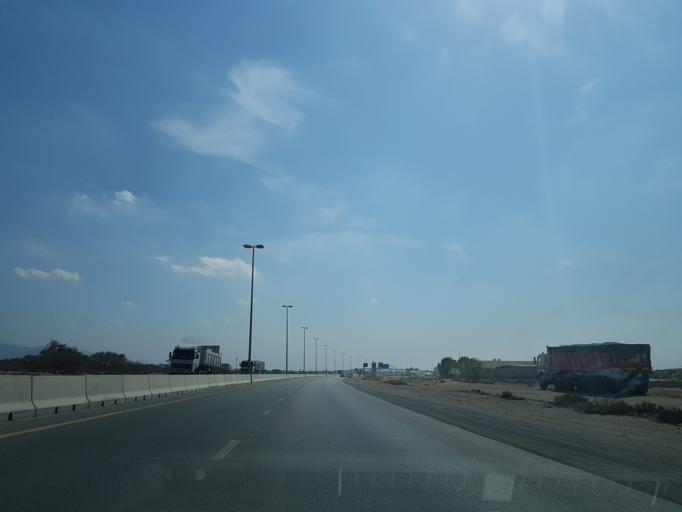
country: AE
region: Ra's al Khaymah
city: Ras al-Khaimah
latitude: 25.8474
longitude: 56.0198
